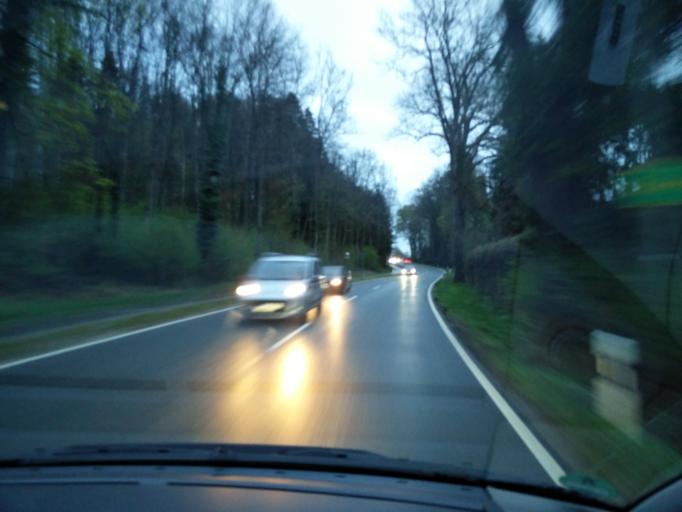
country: DE
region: Bavaria
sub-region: Upper Bavaria
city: Prien am Chiemsee
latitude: 47.8607
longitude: 12.3392
